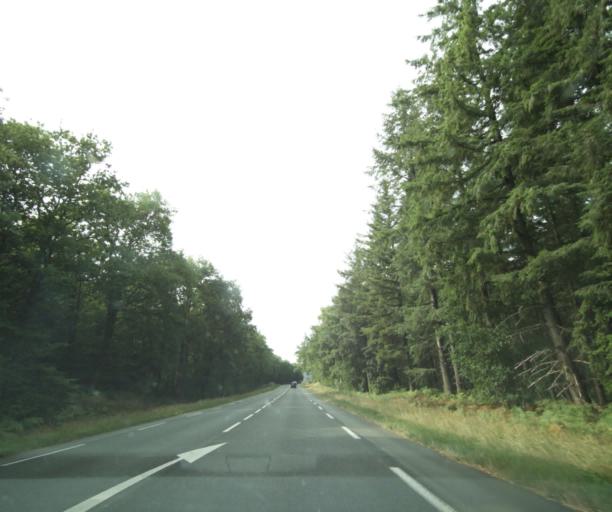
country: FR
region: Pays de la Loire
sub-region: Departement de la Sarthe
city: Marigne-Laille
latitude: 47.7706
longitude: 0.3488
